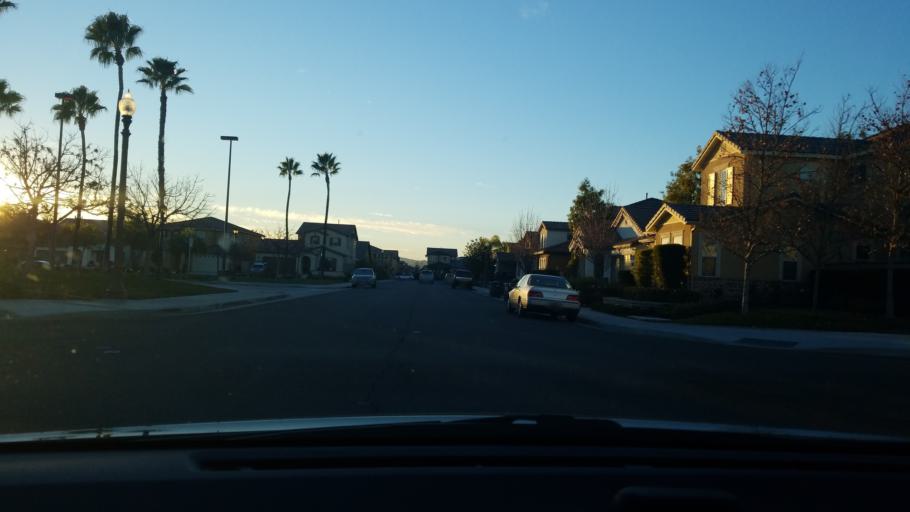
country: US
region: California
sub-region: Riverside County
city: Murrieta Hot Springs
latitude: 33.5529
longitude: -117.1109
